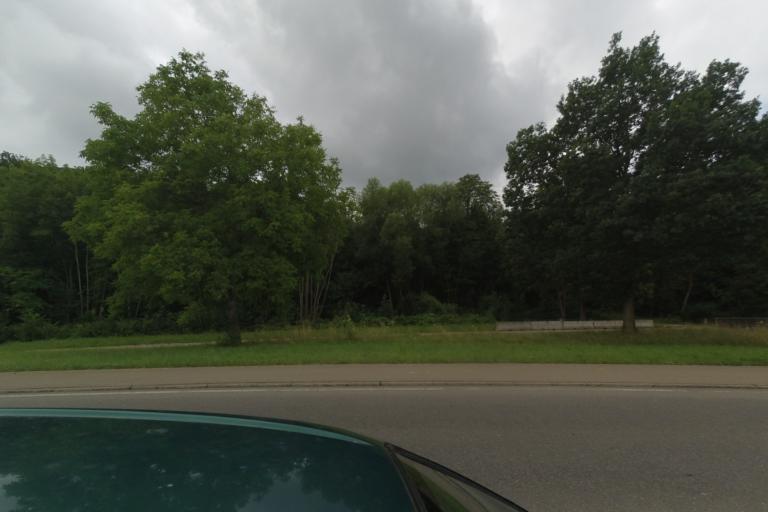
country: DE
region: Baden-Wuerttemberg
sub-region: Regierungsbezirk Stuttgart
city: Kuchen
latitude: 48.6424
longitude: 9.7902
